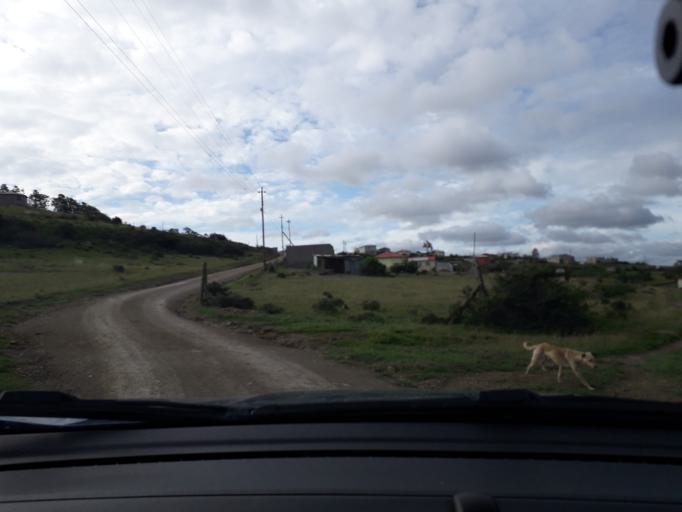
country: ZA
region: Eastern Cape
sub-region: Buffalo City Metropolitan Municipality
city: East London
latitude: -32.8023
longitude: 27.9617
